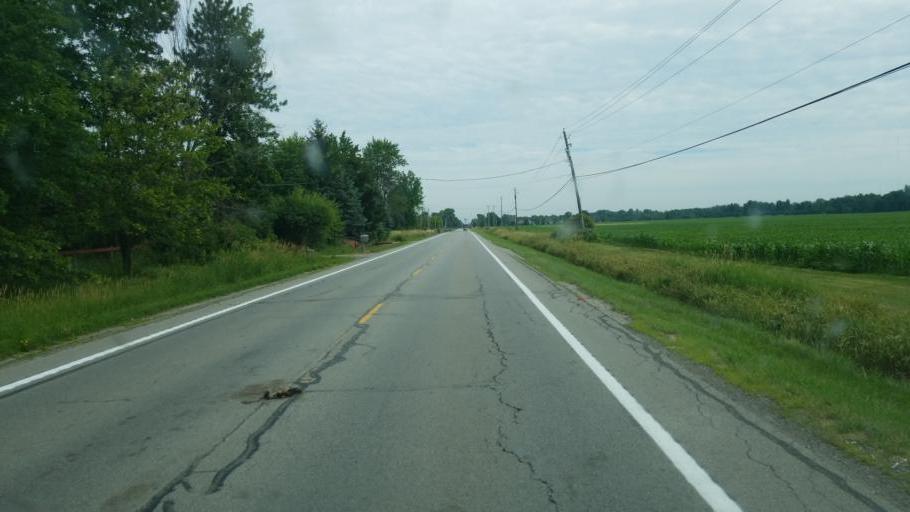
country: US
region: Ohio
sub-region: Lorain County
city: Grafton
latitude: 41.2474
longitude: -82.0227
